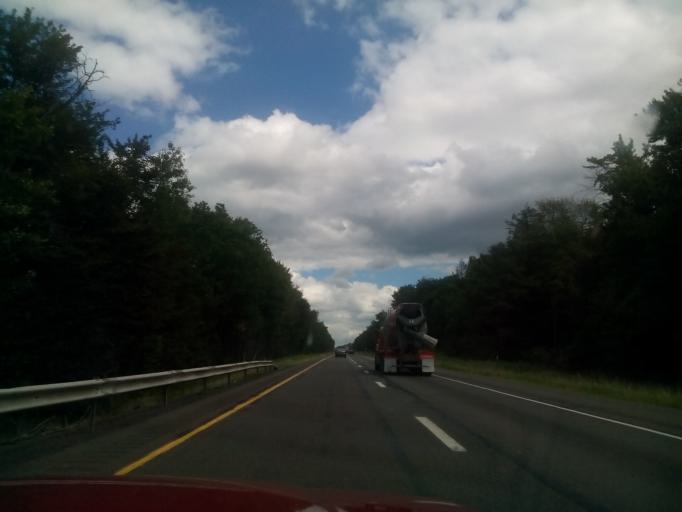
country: US
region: Pennsylvania
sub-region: Carbon County
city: Towamensing Trails
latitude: 41.0761
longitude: -75.5523
